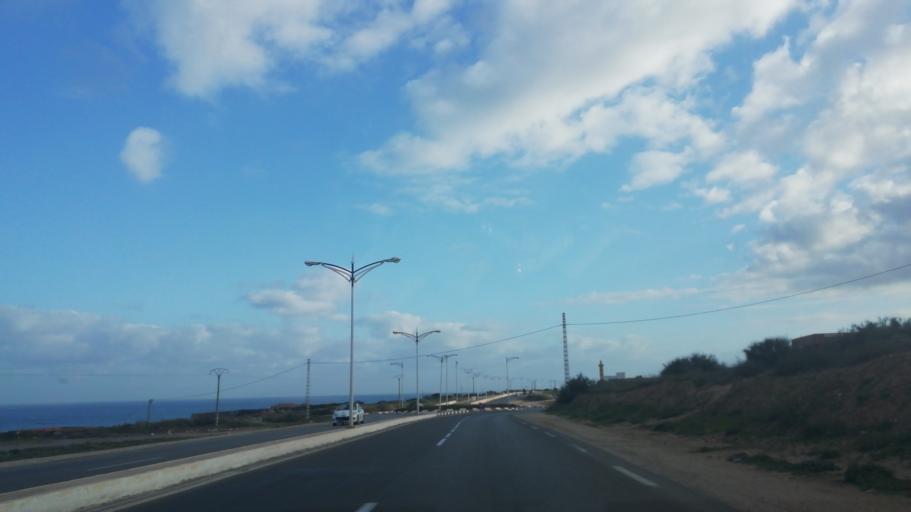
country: DZ
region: Mostaganem
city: Mostaganem
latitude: 36.0644
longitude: 0.1692
